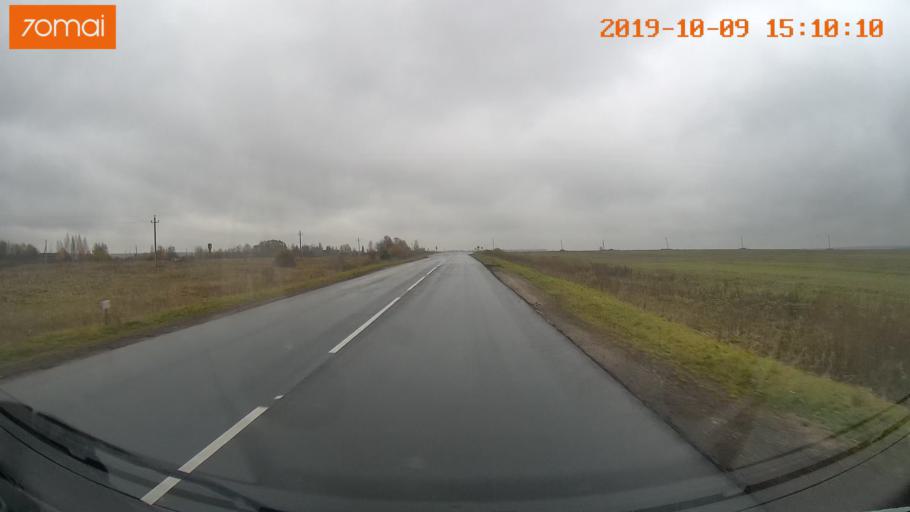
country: RU
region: Kostroma
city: Susanino
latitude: 58.1815
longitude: 41.6438
